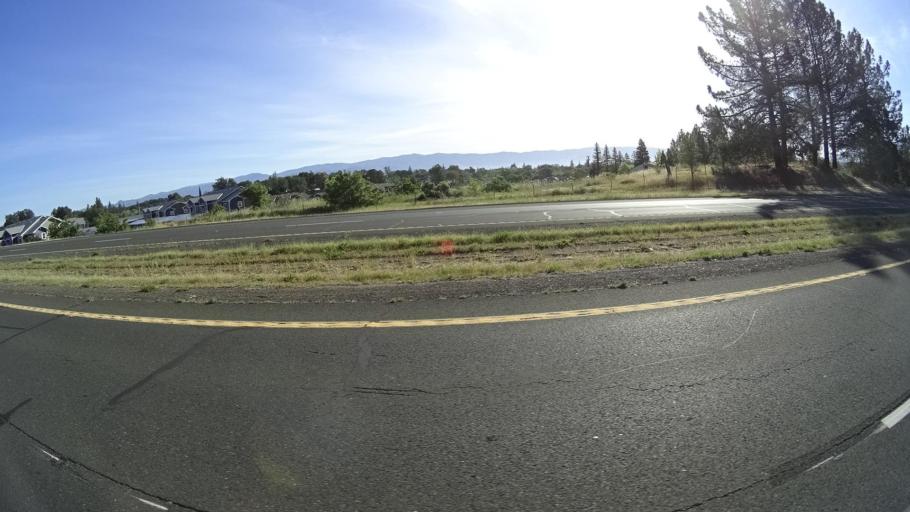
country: US
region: California
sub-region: Lake County
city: Lakeport
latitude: 39.0385
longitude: -122.9284
